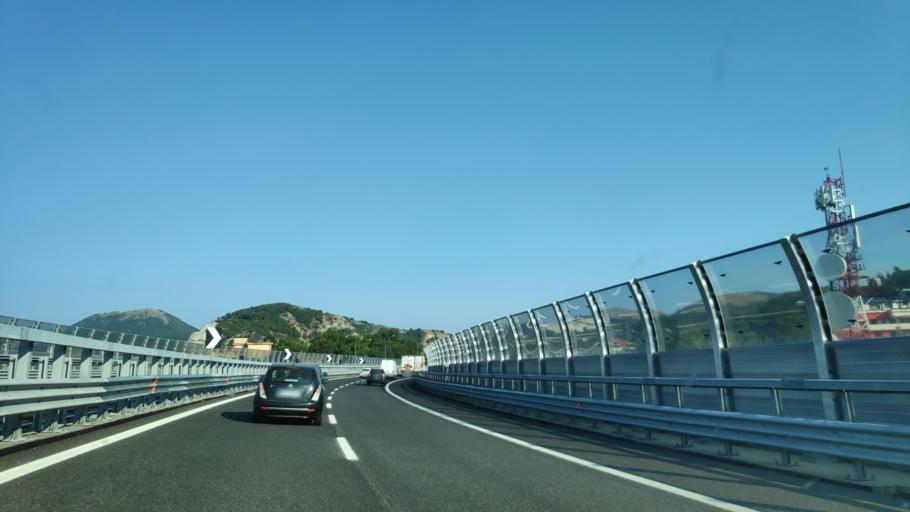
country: IT
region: Basilicate
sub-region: Provincia di Potenza
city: Lagonegro
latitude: 40.1313
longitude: 15.7629
